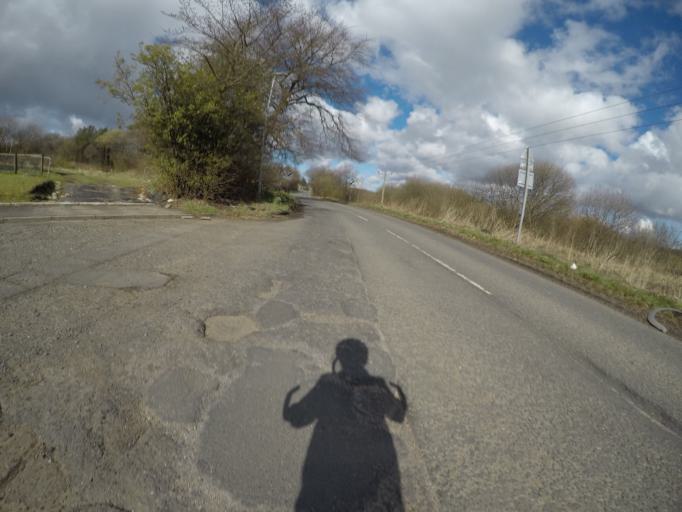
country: GB
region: Scotland
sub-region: North Ayrshire
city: Beith
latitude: 55.7312
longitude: -4.6068
